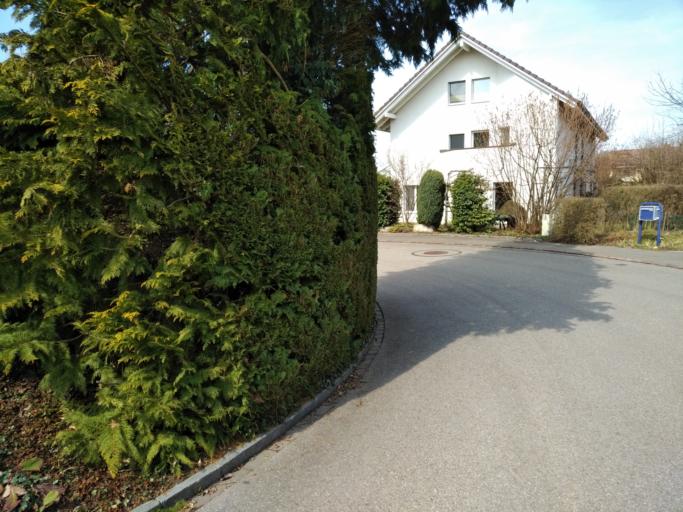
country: CH
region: Zurich
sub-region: Bezirk Winterthur
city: Wiesendangen / Wiesendangen (Dorf)
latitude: 47.5192
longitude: 8.7918
